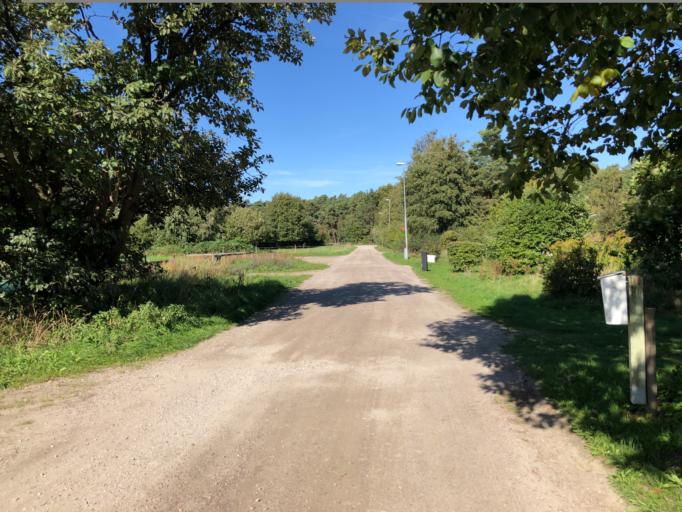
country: SE
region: Skane
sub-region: Lomma Kommun
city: Lomma
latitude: 55.6866
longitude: 13.0706
